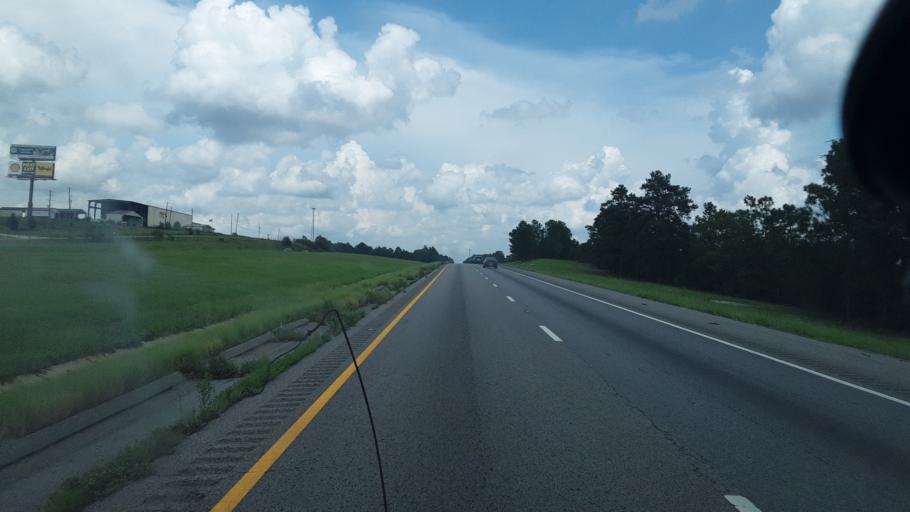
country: US
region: South Carolina
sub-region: Kershaw County
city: Elgin
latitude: 34.1569
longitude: -80.7299
